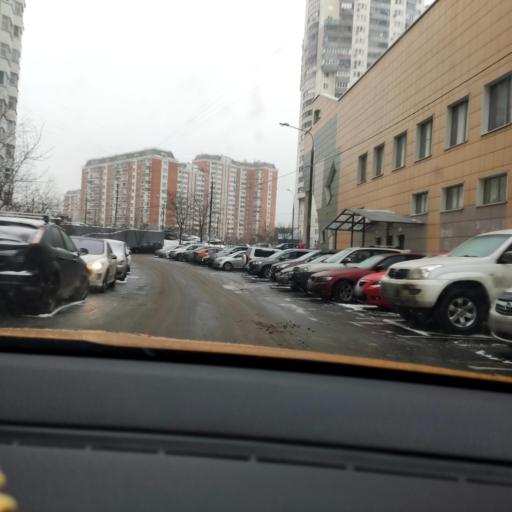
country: RU
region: Moscow
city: Nekrasovka
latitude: 55.7233
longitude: 37.9098
